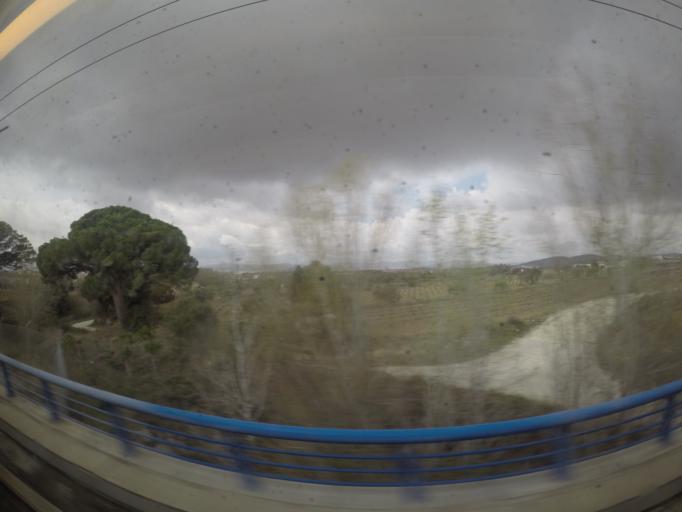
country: ES
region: Catalonia
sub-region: Provincia de Barcelona
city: Castellet
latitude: 41.3017
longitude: 1.6378
